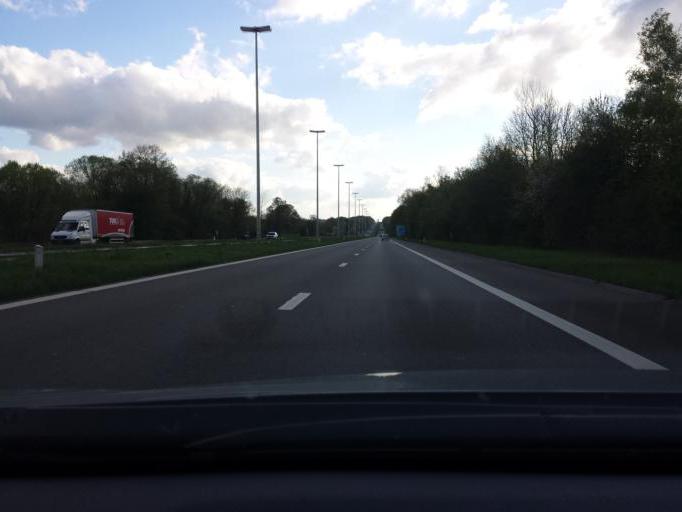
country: BE
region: Wallonia
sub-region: Province de Liege
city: Raeren
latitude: 50.7085
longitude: 6.0991
